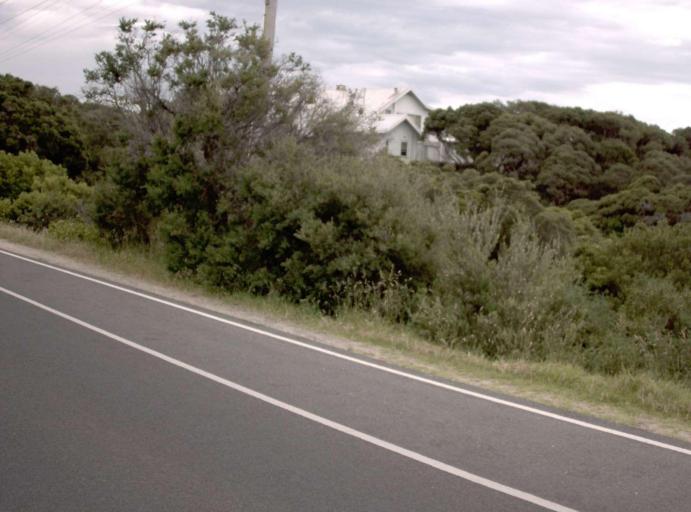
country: AU
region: Victoria
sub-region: Mornington Peninsula
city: Sorrento
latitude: -38.3459
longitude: 144.7555
